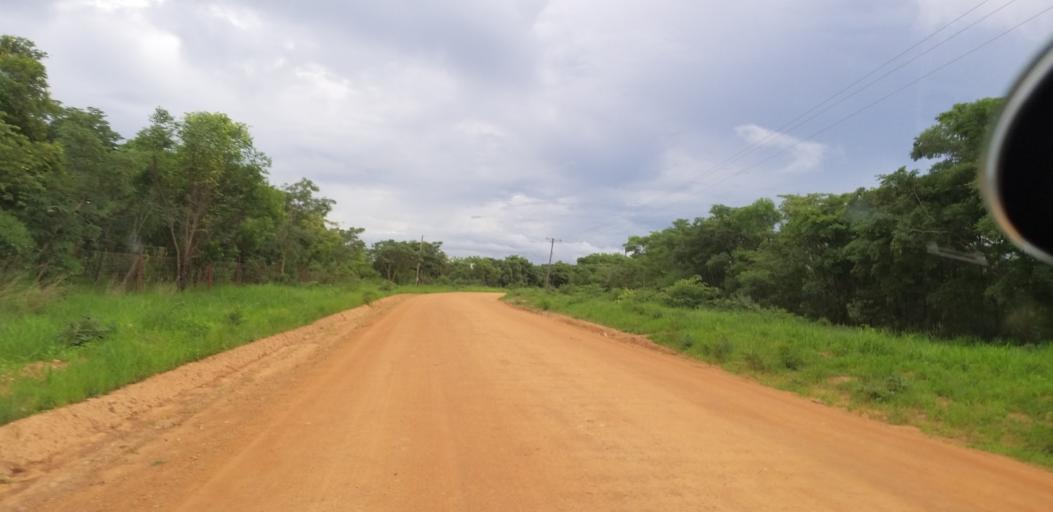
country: ZM
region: Lusaka
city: Chongwe
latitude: -15.1767
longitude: 28.4607
